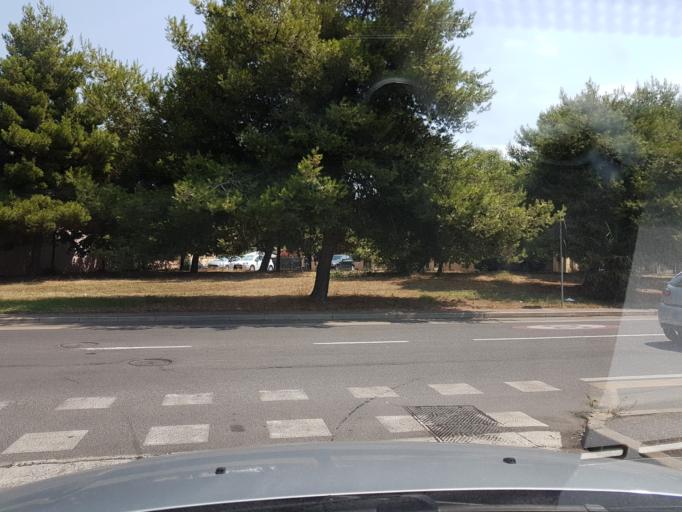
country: IT
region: Sardinia
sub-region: Provincia di Oristano
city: Oristano
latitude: 39.9138
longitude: 8.5893
